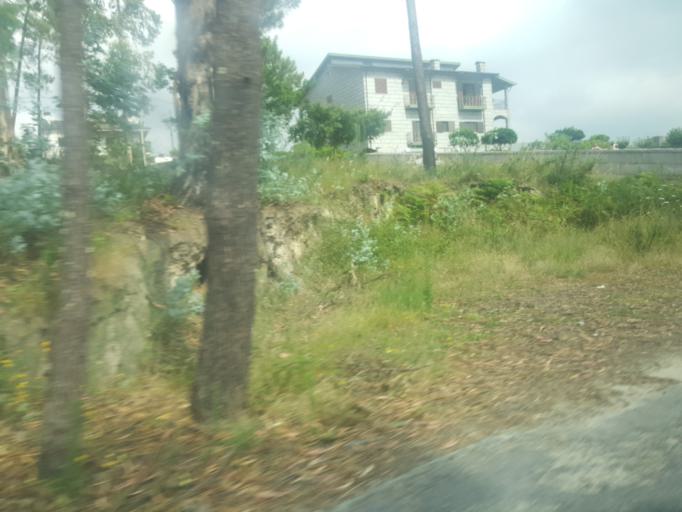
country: PT
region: Porto
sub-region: Marco de Canaveses
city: Marco de Canavezes
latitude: 41.1763
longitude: -8.1919
